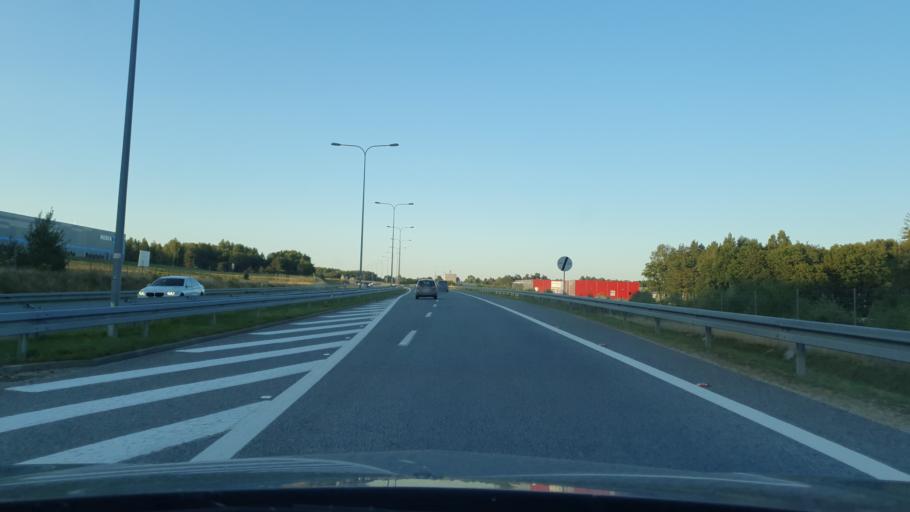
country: PL
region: Pomeranian Voivodeship
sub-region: Slupsk
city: Slupsk
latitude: 54.4443
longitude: 17.0784
